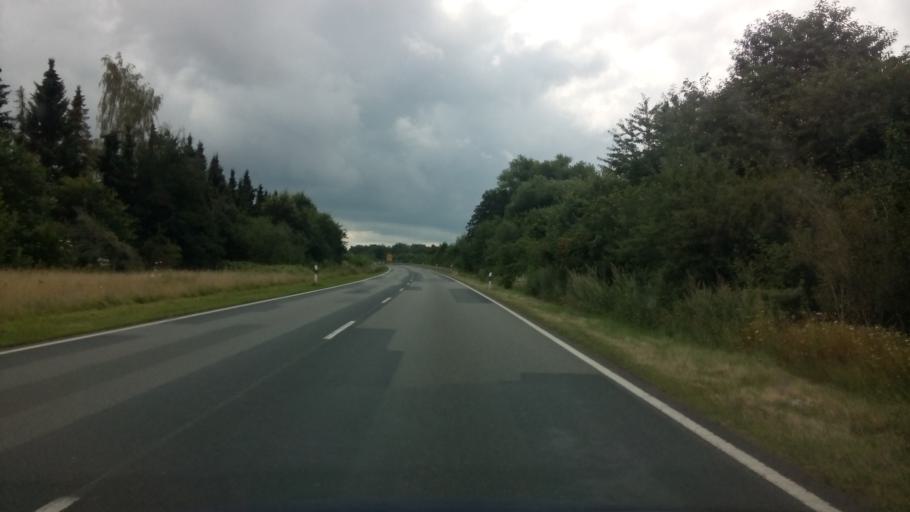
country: DE
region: Lower Saxony
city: Diepholz
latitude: 52.6168
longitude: 8.3630
